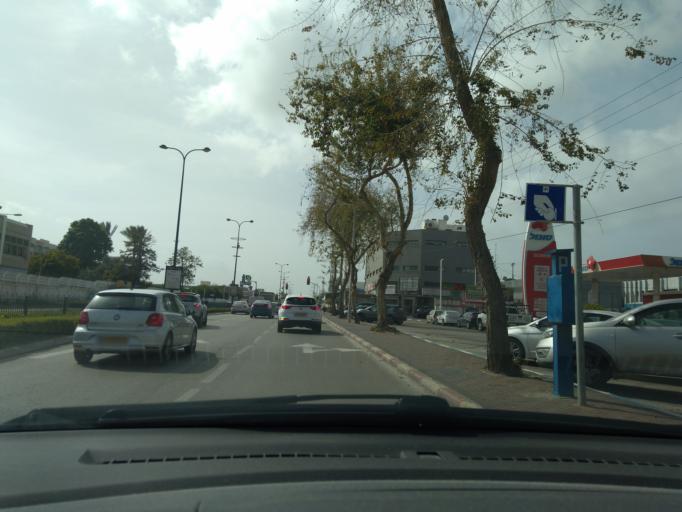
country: IL
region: Central District
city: Even Yehuda
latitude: 32.2841
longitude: 34.8621
